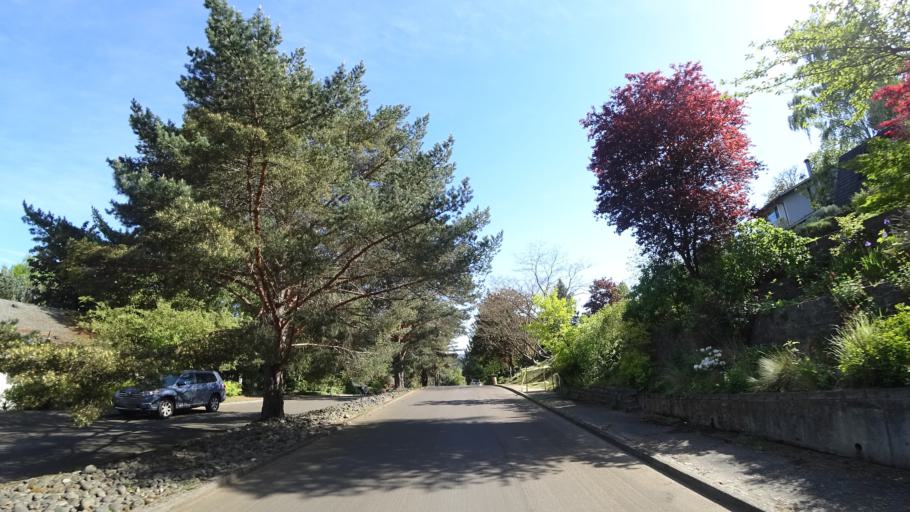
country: US
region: Oregon
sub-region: Washington County
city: West Slope
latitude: 45.4978
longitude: -122.7470
